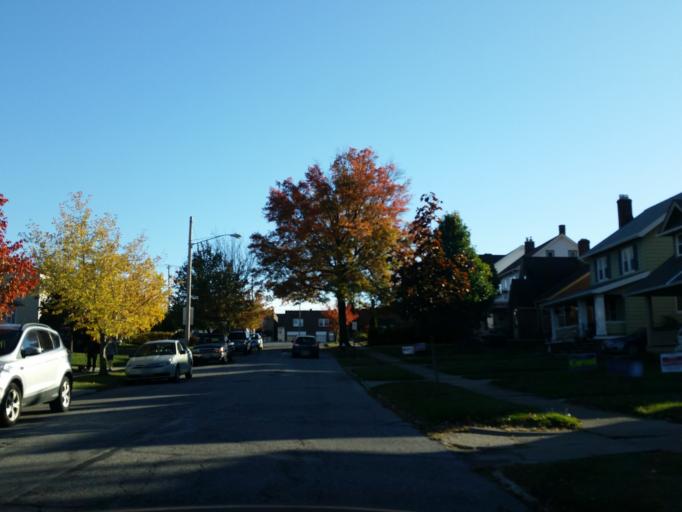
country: US
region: Ohio
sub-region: Cuyahoga County
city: Lakewood
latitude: 41.4783
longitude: -81.7842
